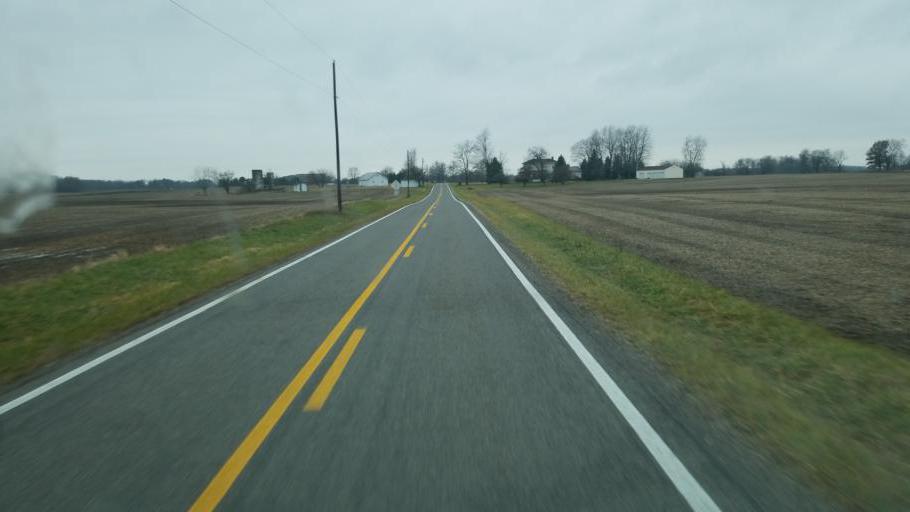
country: US
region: Ohio
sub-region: Delaware County
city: Ashley
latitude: 40.3580
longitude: -83.0031
